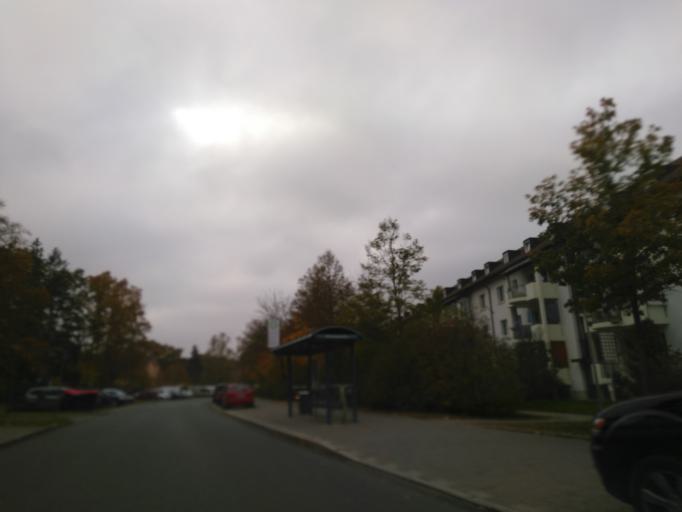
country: DE
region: Bavaria
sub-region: Upper Bavaria
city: Unterhaching
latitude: 48.0911
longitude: 11.5971
